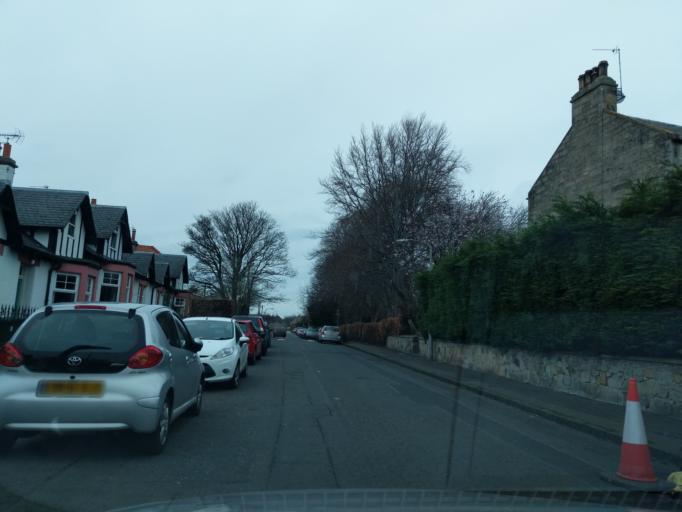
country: GB
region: Scotland
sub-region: Edinburgh
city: Colinton
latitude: 55.9379
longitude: -3.2859
